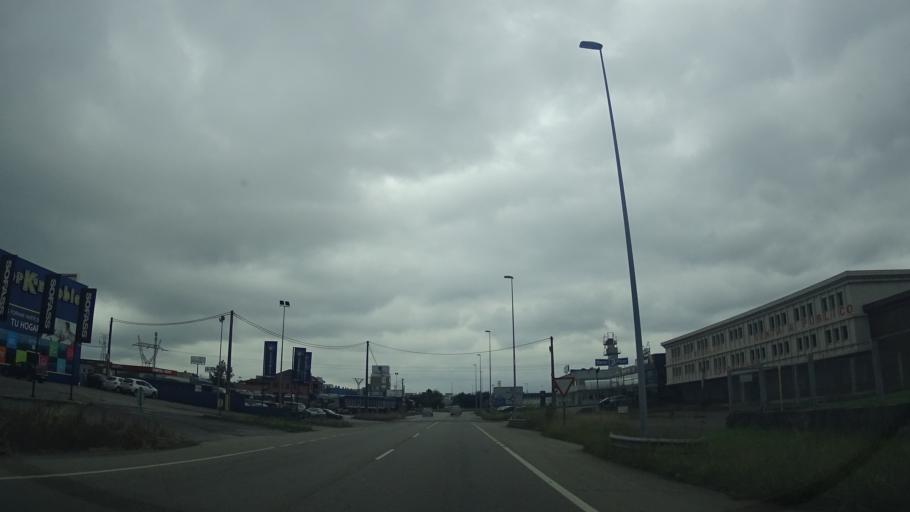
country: ES
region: Asturias
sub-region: Province of Asturias
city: Lugones
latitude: 43.3836
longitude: -5.7608
